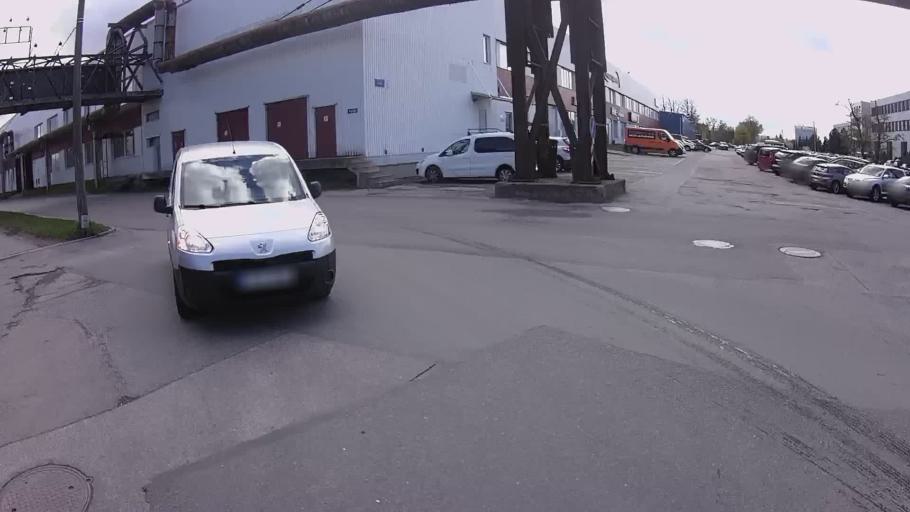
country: EE
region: Harju
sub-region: Tallinna linn
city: Tallinn
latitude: 59.4207
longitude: 24.6846
